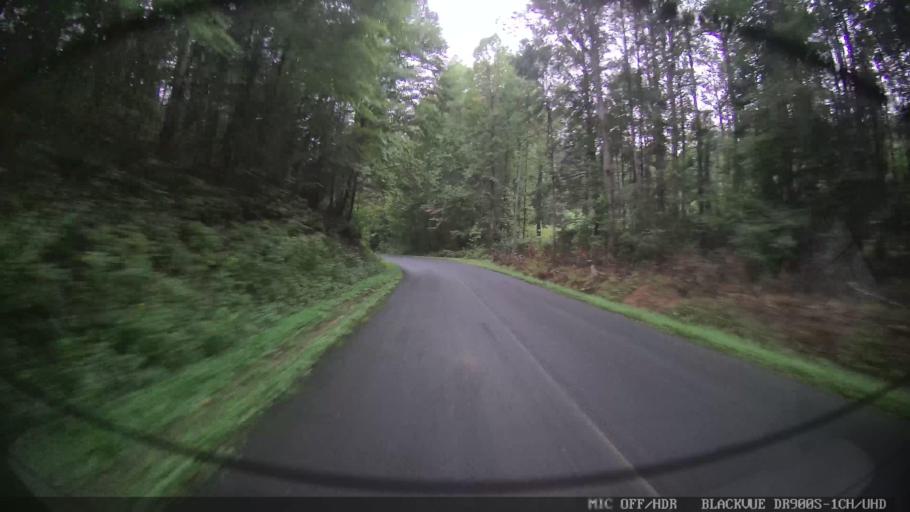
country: US
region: Georgia
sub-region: Gilmer County
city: Ellijay
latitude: 34.7946
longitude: -84.5580
